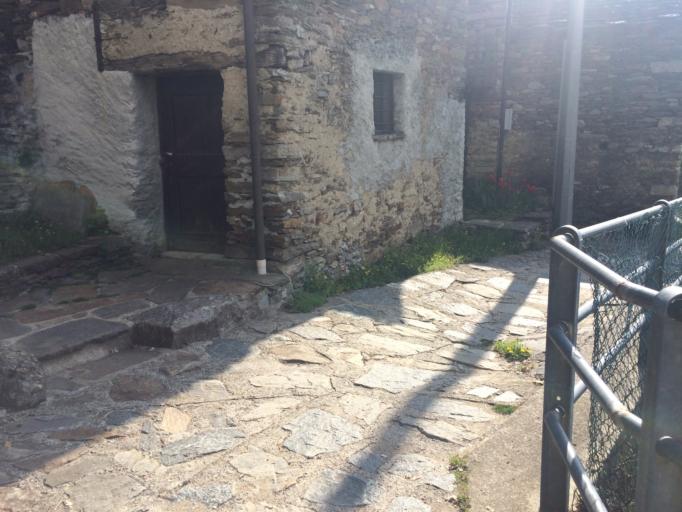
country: IT
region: Piedmont
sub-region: Provincia Verbano-Cusio-Ossola
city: Gurro
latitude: 46.0752
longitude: 8.5719
